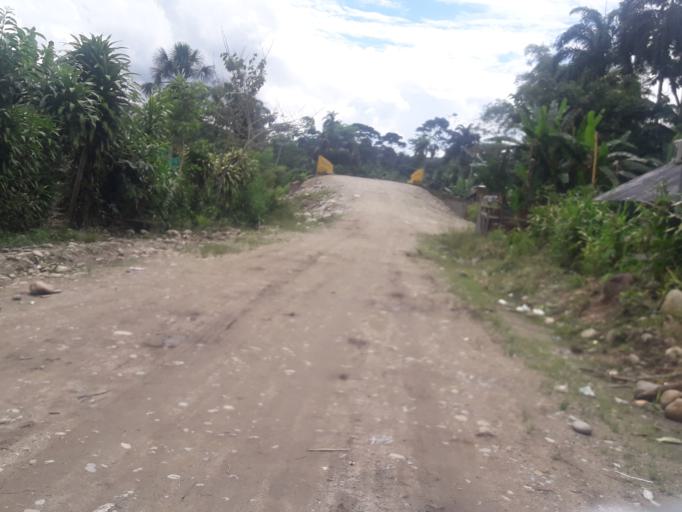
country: EC
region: Napo
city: Tena
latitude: -0.9771
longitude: -77.8519
